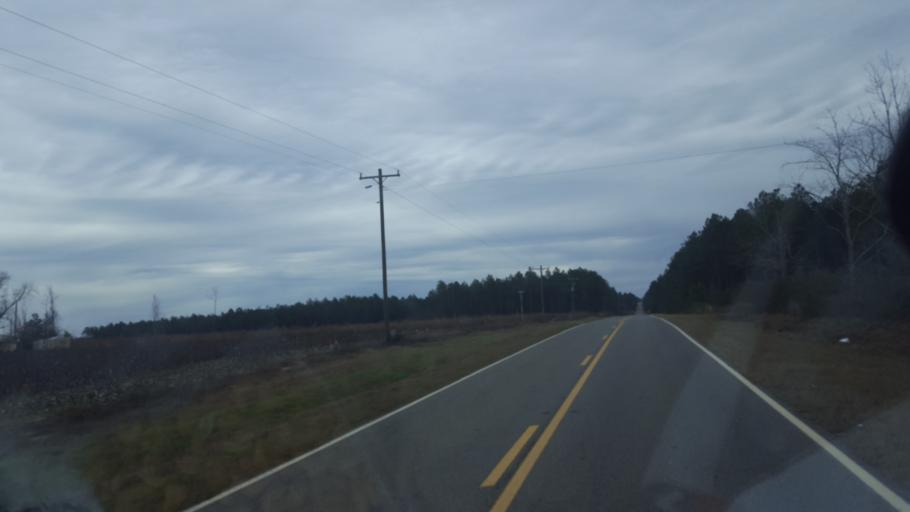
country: US
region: Georgia
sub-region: Wilcox County
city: Rochelle
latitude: 31.7830
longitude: -83.4138
